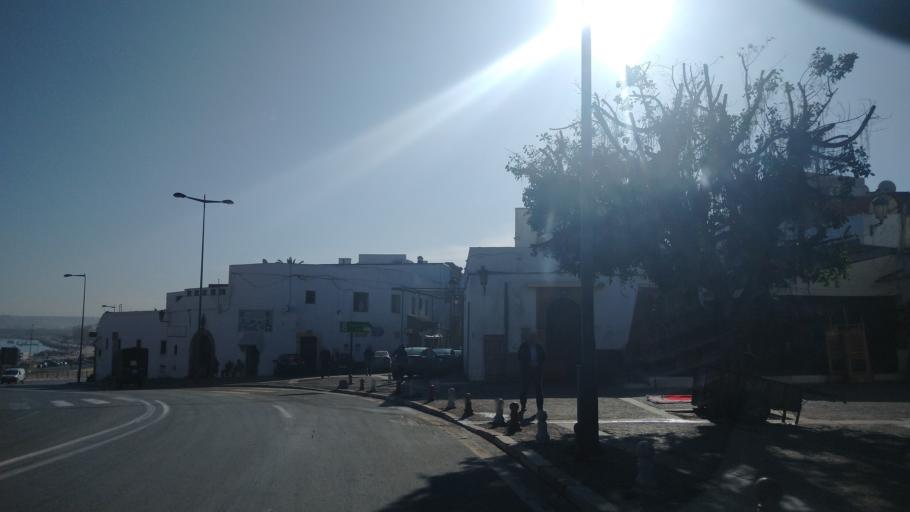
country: MA
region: Rabat-Sale-Zemmour-Zaer
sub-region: Rabat
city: Rabat
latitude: 34.0294
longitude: -6.8355
